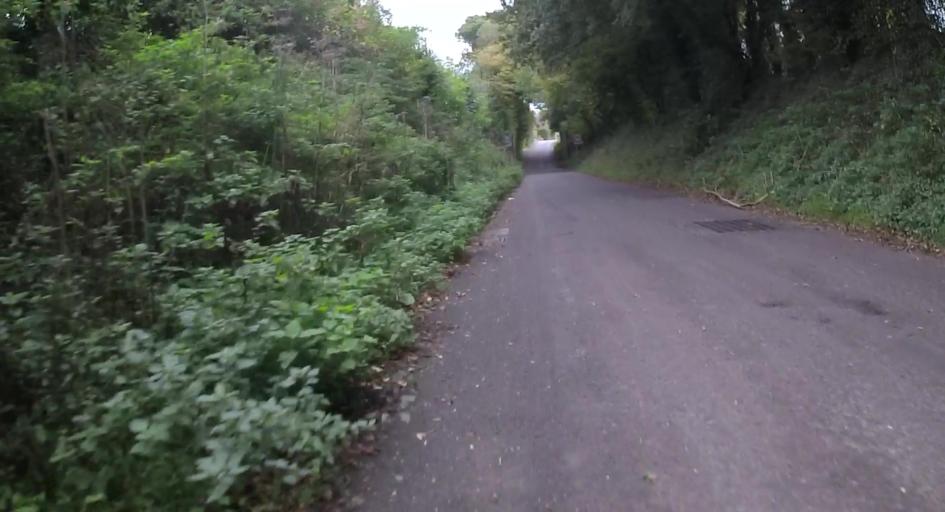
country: GB
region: England
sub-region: Hampshire
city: Alton
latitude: 51.1100
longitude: -0.9976
